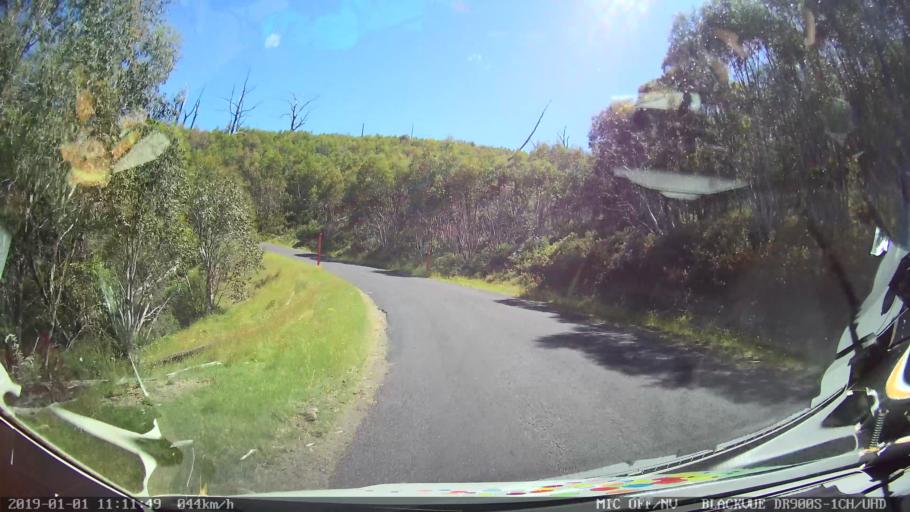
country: AU
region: New South Wales
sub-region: Snowy River
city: Jindabyne
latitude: -35.9598
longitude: 148.4020
